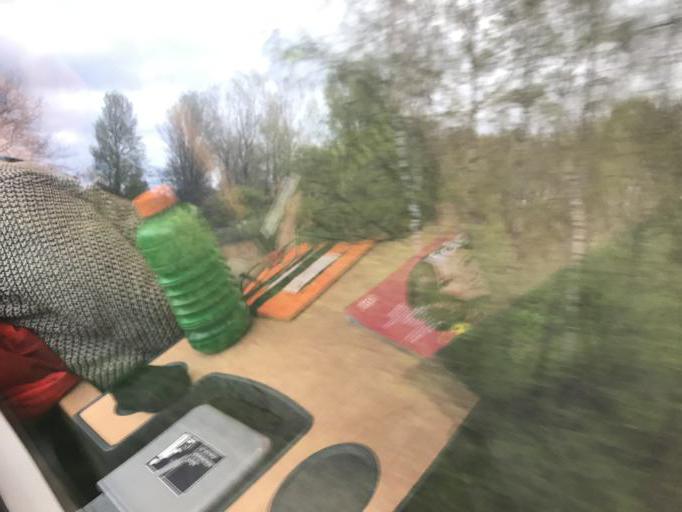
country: DE
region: Schleswig-Holstein
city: Neumunster
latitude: 54.0601
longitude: 9.9602
